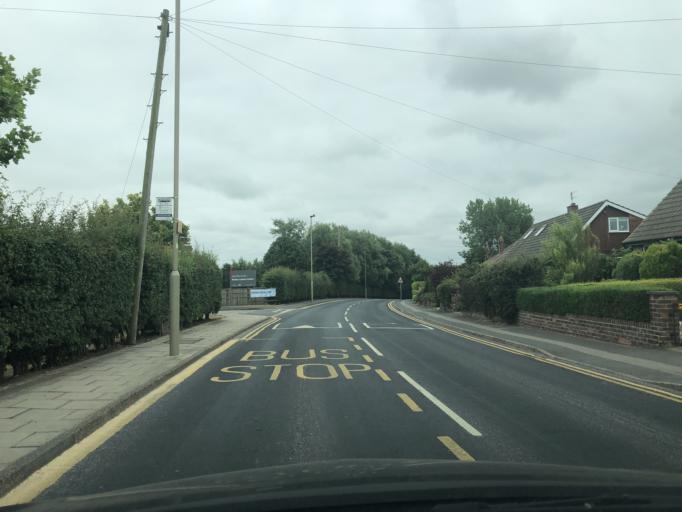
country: GB
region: England
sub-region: North Yorkshire
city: Scarborough
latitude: 54.2385
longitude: -0.3952
